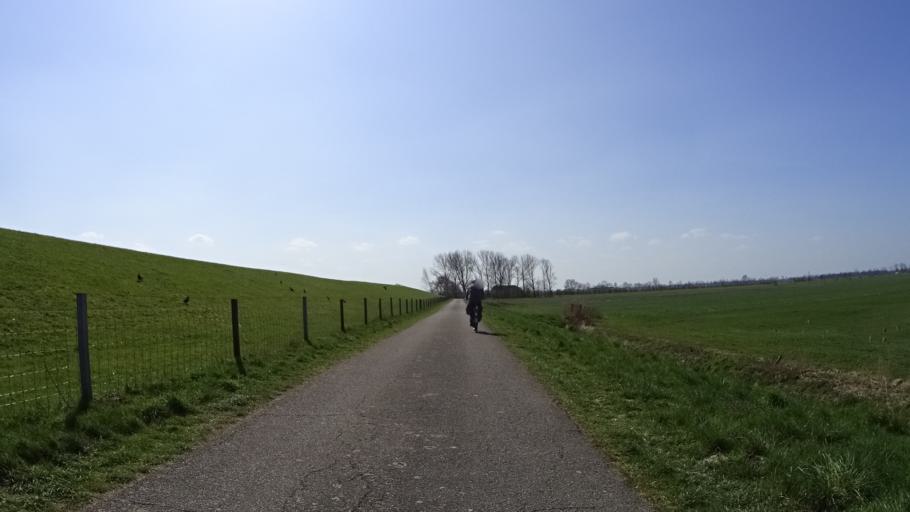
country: DE
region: Lower Saxony
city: Weener
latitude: 53.1369
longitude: 7.3648
